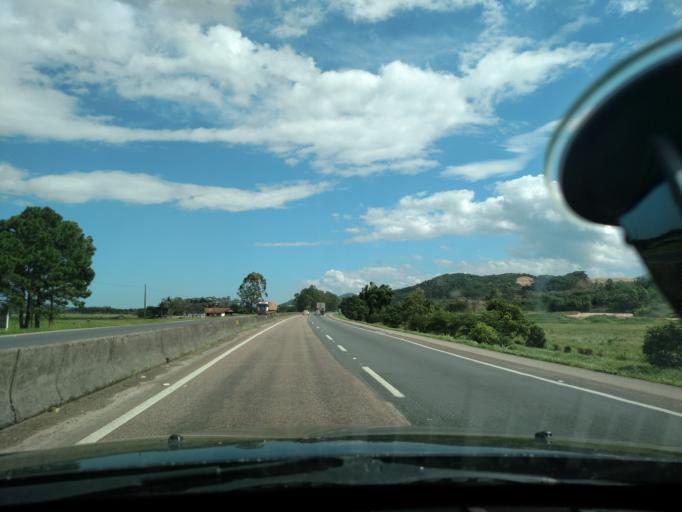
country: BR
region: Santa Catarina
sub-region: Tijucas
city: Tijucas
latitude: -27.3541
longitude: -48.6323
